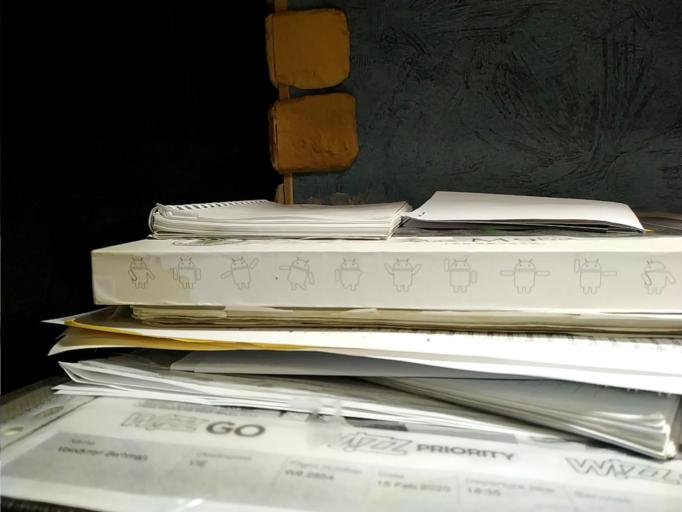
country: RU
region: Arkhangelskaya
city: Konevo
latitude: 62.8078
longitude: 38.5532
